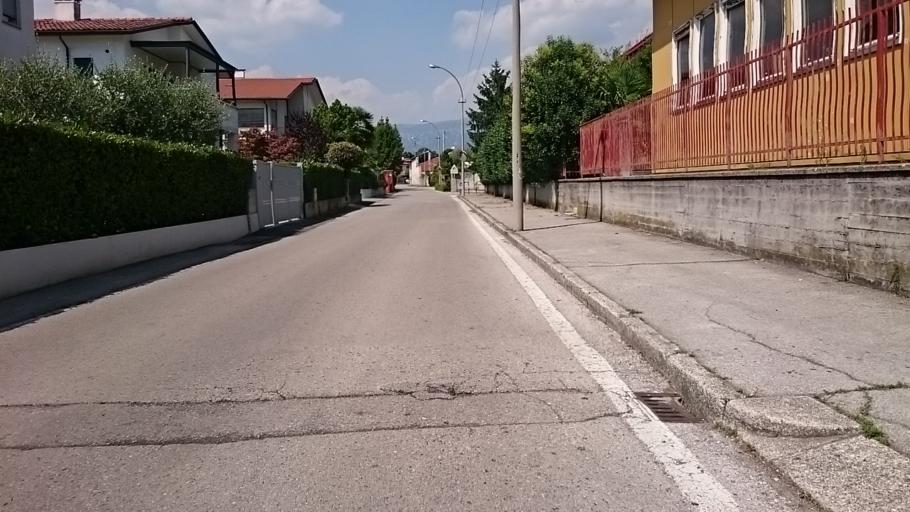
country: IT
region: Veneto
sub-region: Provincia di Vicenza
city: Bassano del Grappa
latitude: 45.7494
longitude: 11.7301
